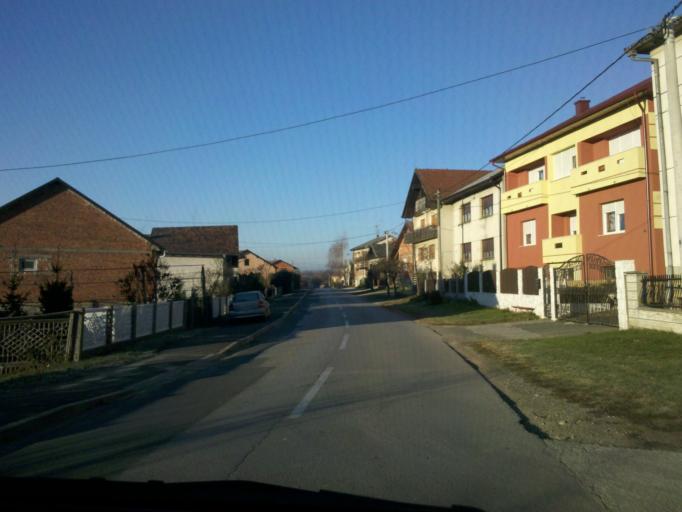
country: HR
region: Medimurska
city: Belica
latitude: 46.4060
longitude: 16.5165
